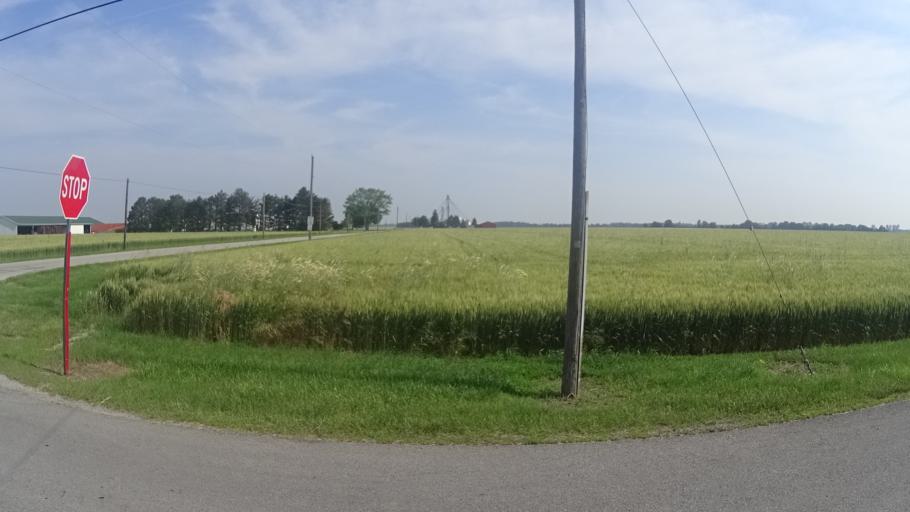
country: US
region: Ohio
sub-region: Huron County
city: Bellevue
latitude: 41.2986
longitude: -82.7920
